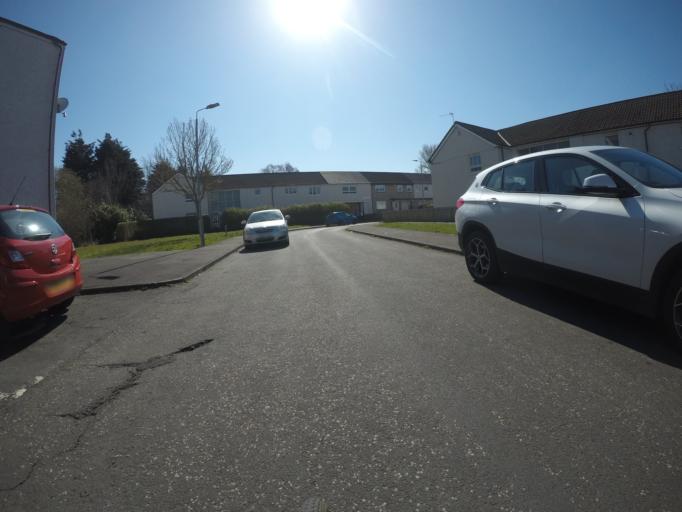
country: GB
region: Scotland
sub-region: North Ayrshire
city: Irvine
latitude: 55.6281
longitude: -4.6564
